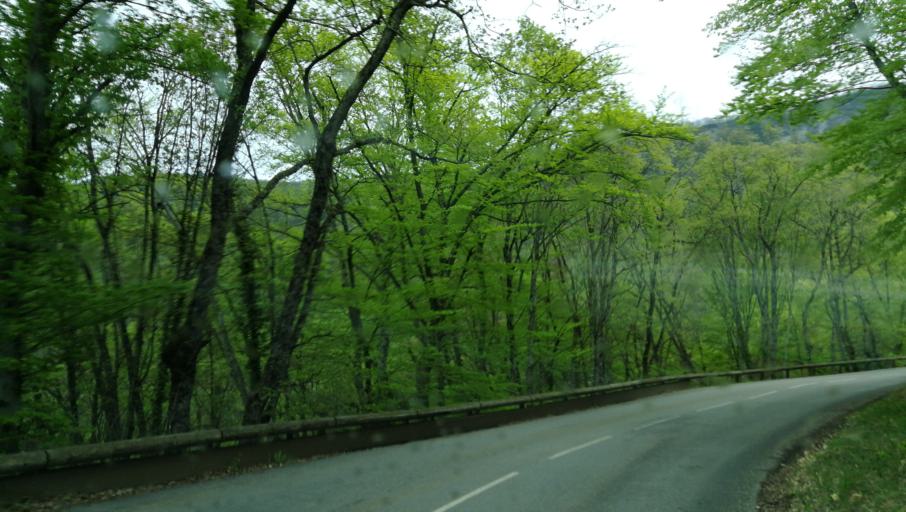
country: FR
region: Rhone-Alpes
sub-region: Departement de la Drome
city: Saint-Jean-en-Royans
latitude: 44.9975
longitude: 5.2933
